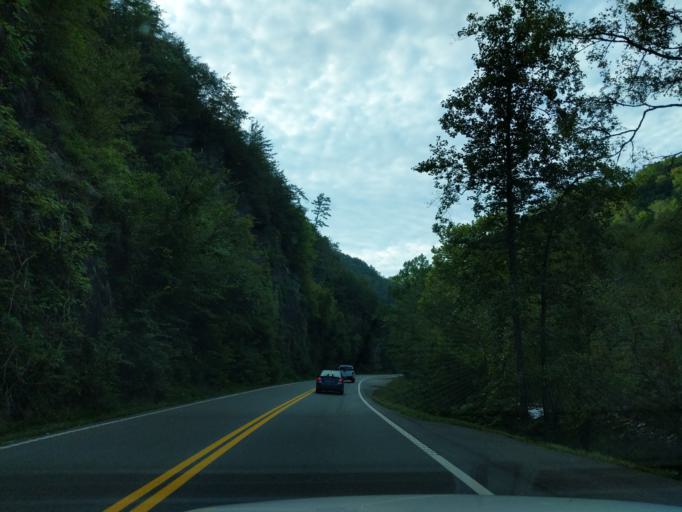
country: US
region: Tennessee
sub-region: Polk County
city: Benton
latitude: 35.0933
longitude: -84.5323
